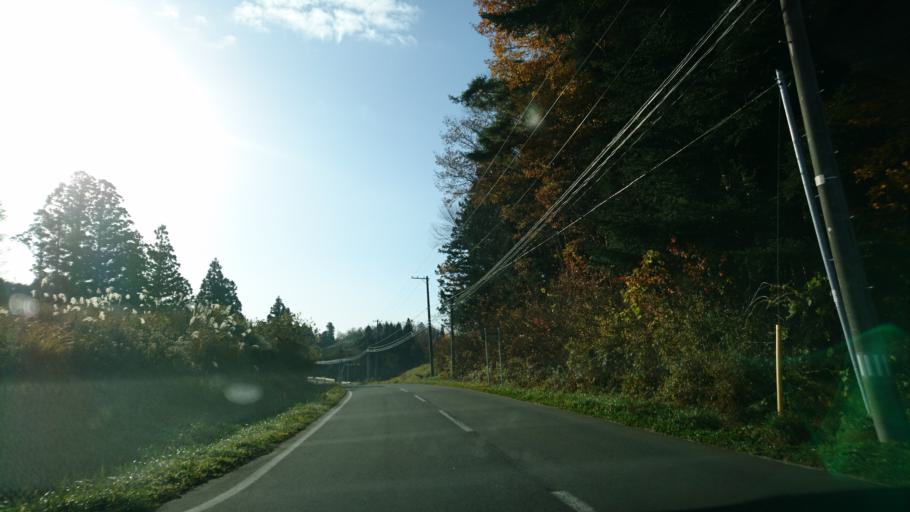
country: JP
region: Iwate
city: Ichinoseki
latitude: 38.8783
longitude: 141.2915
